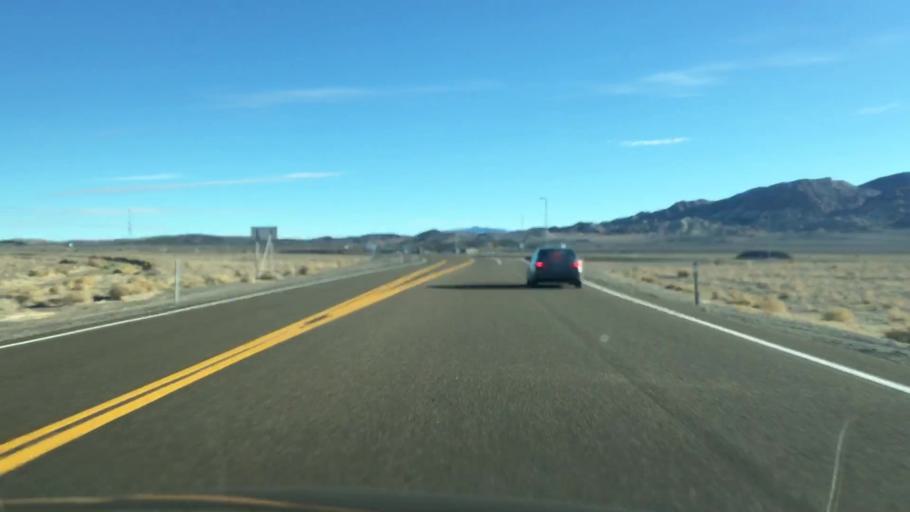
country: US
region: Nevada
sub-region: Nye County
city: Tonopah
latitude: 38.0334
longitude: -117.8881
